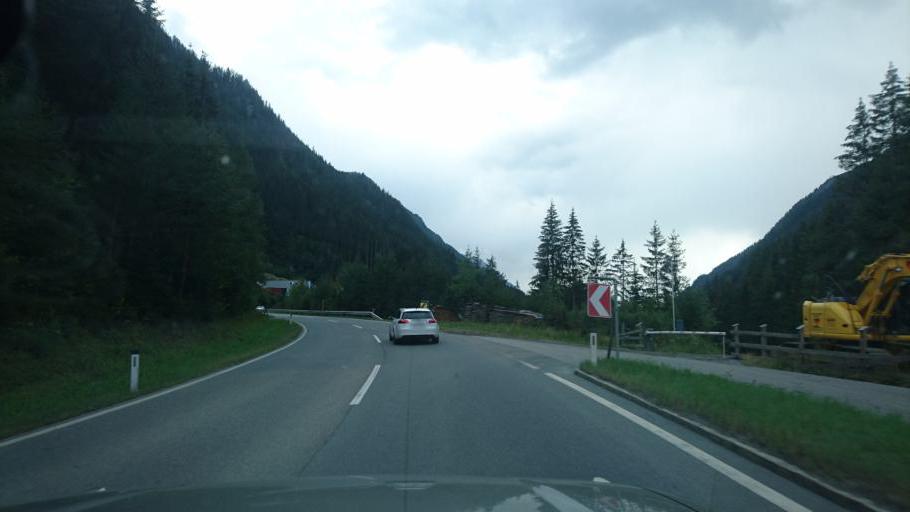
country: AT
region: Tyrol
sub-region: Politischer Bezirk Landeck
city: Ischgl
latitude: 47.0422
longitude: 10.3352
